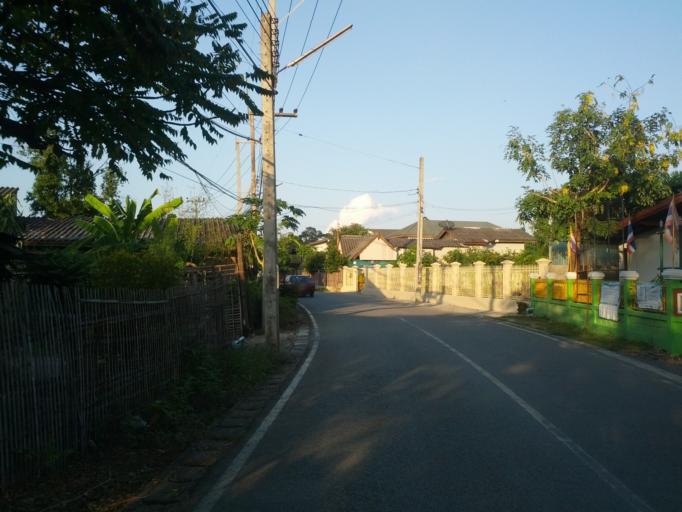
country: TH
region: Chiang Mai
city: San Kamphaeng
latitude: 18.7590
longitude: 99.0836
